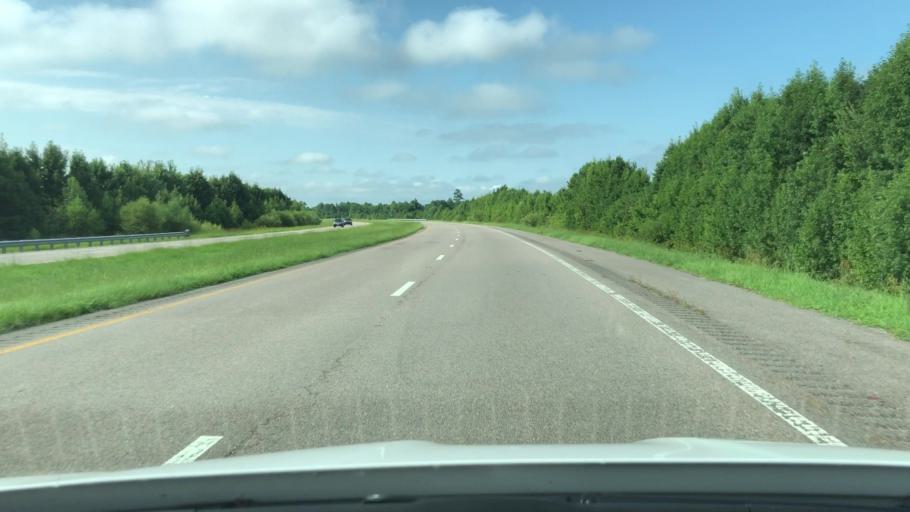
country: US
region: Virginia
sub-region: City of Portsmouth
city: Portsmouth Heights
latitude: 36.6057
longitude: -76.3800
